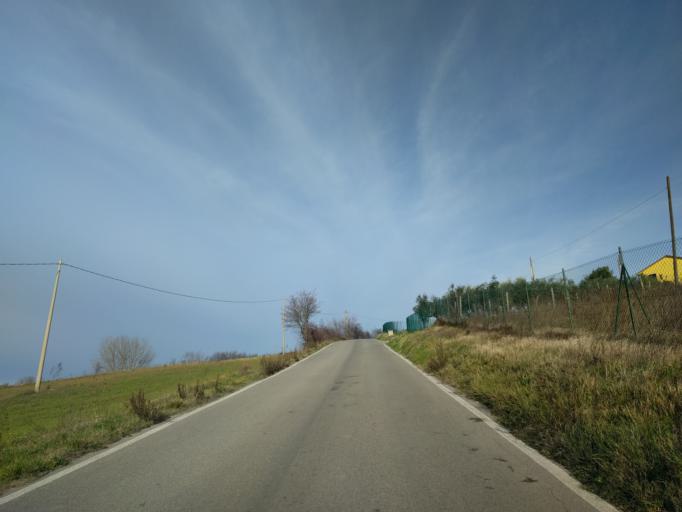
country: IT
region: The Marches
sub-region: Provincia di Pesaro e Urbino
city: Cuccurano
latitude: 43.7982
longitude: 12.9507
